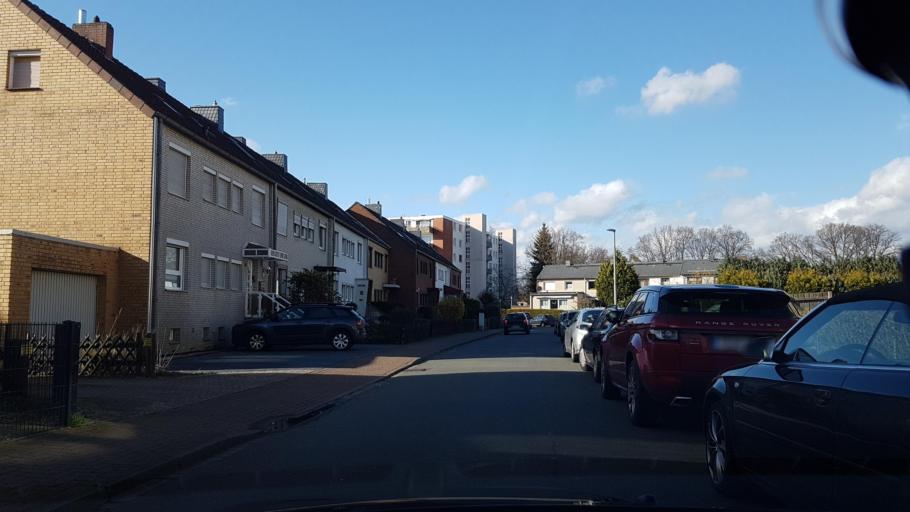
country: DE
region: Lower Saxony
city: Auf der Horst
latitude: 52.4104
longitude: 9.6044
